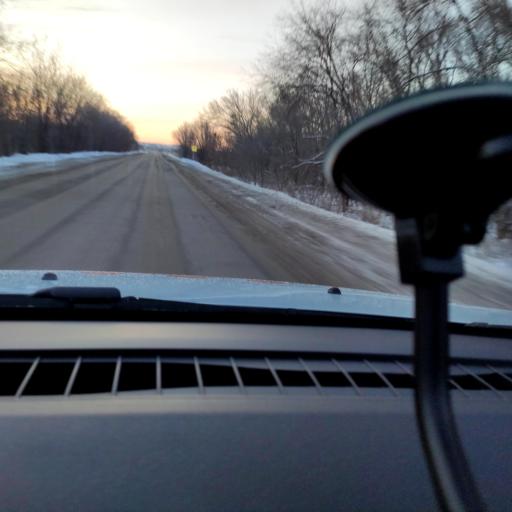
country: RU
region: Samara
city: Samara
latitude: 53.0957
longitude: 50.2300
